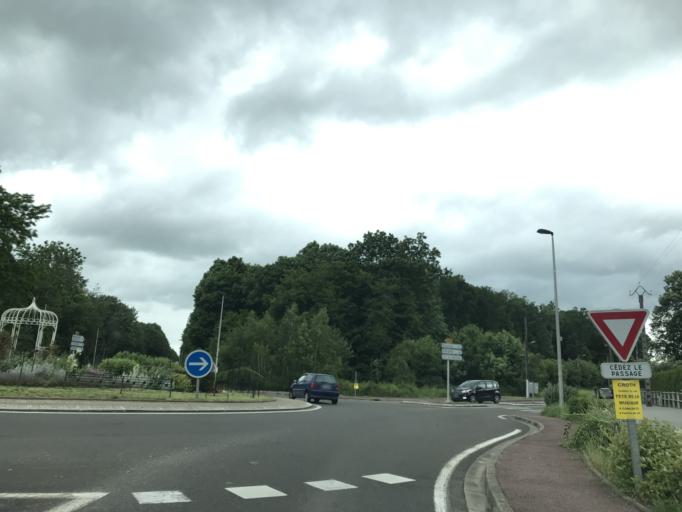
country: FR
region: Haute-Normandie
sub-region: Departement de l'Eure
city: La Couture-Boussey
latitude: 48.9016
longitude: 1.3968
